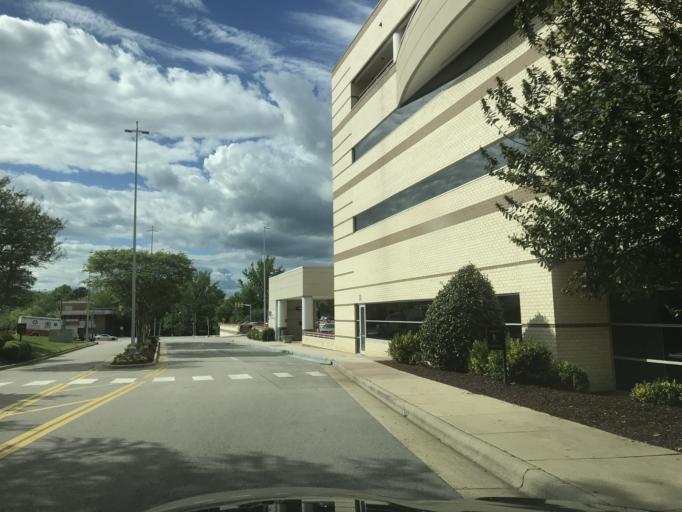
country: US
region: North Carolina
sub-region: Wake County
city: Raleigh
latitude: 35.7858
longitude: -78.5876
